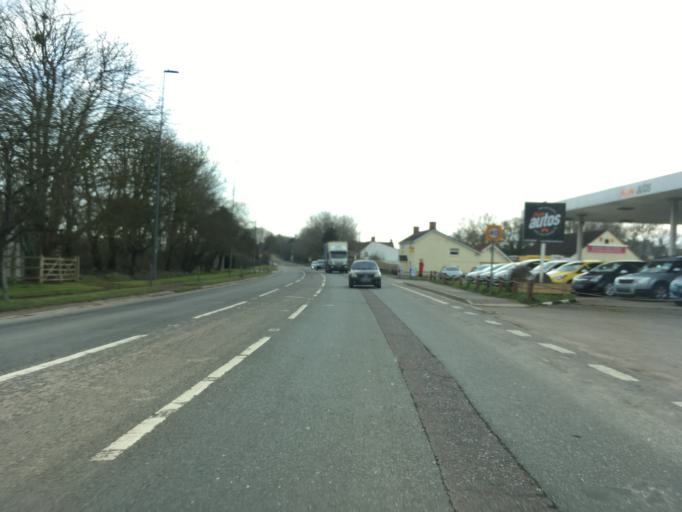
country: GB
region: England
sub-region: South Gloucestershire
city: Falfield
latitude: 51.6357
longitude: -2.4600
